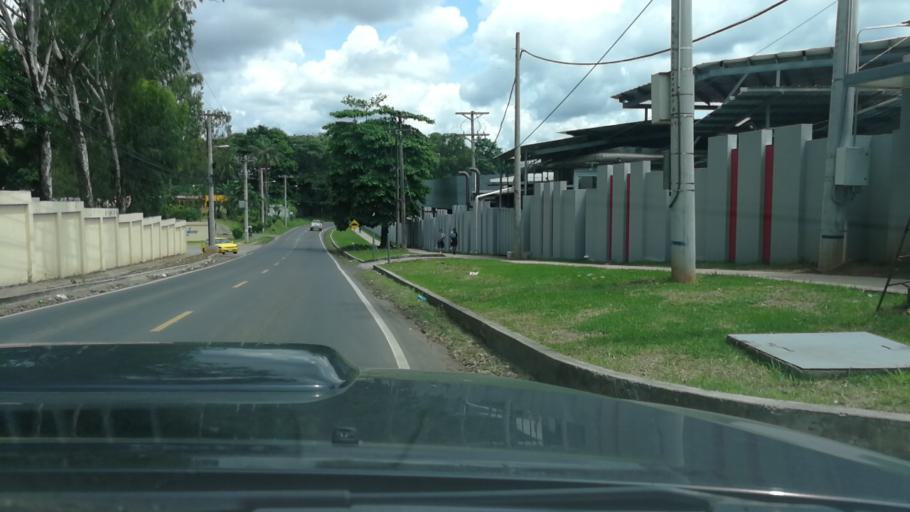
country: PA
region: Panama
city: Tocumen
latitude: 9.0744
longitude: -79.4280
